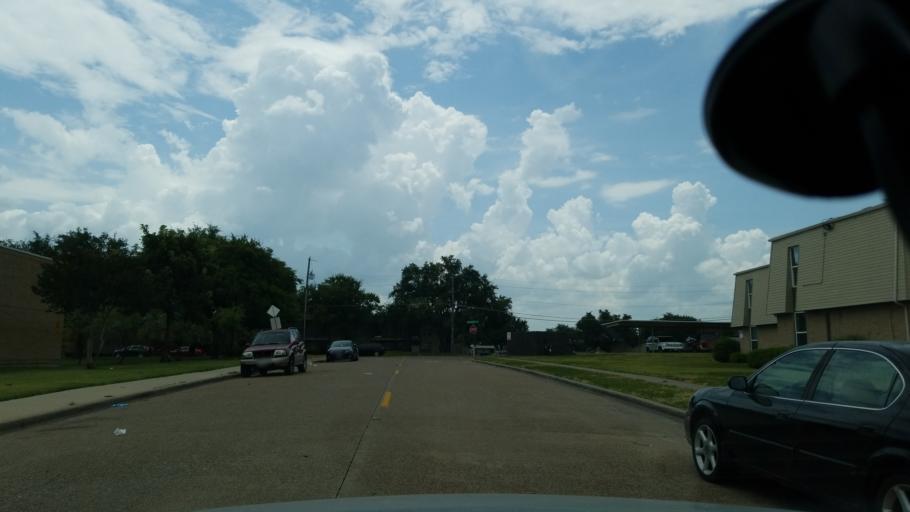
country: US
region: Texas
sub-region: Dallas County
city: Cockrell Hill
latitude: 32.6836
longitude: -96.8554
